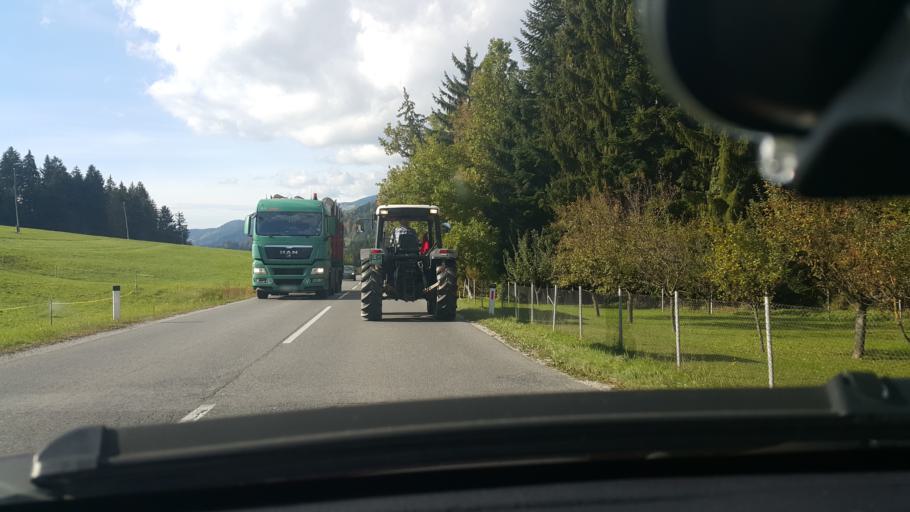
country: SI
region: Vitanje
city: Vitanje
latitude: 46.3780
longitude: 15.3321
